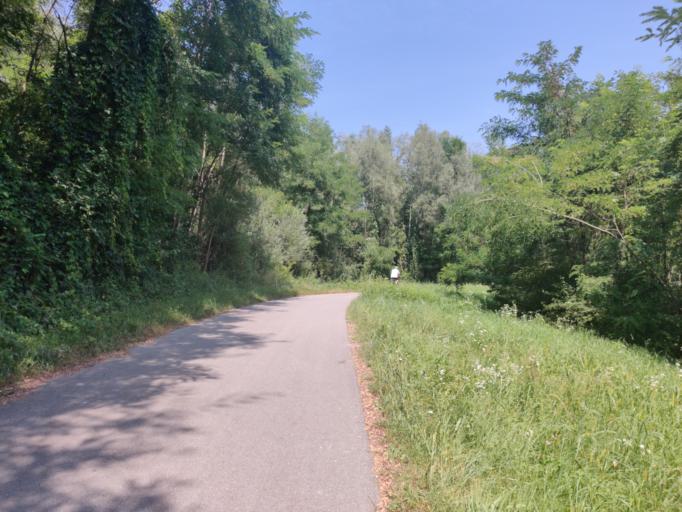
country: AT
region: Upper Austria
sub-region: Politischer Bezirk Urfahr-Umgebung
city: Goldworth
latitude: 48.3181
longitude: 14.1384
